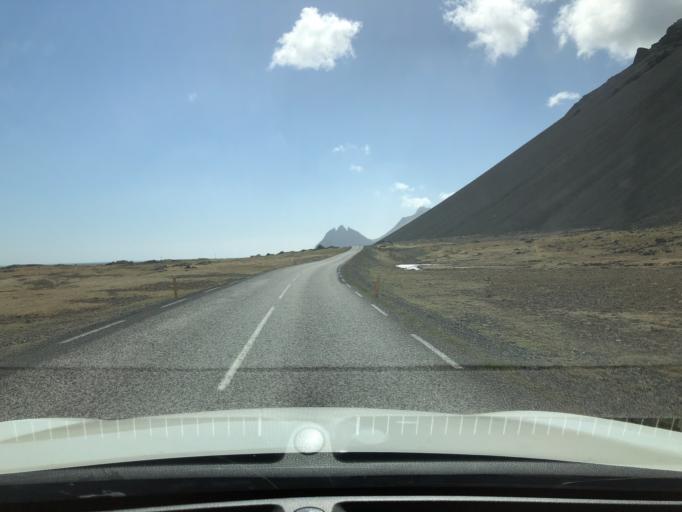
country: IS
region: East
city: Hoefn
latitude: 64.3600
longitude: -14.9239
